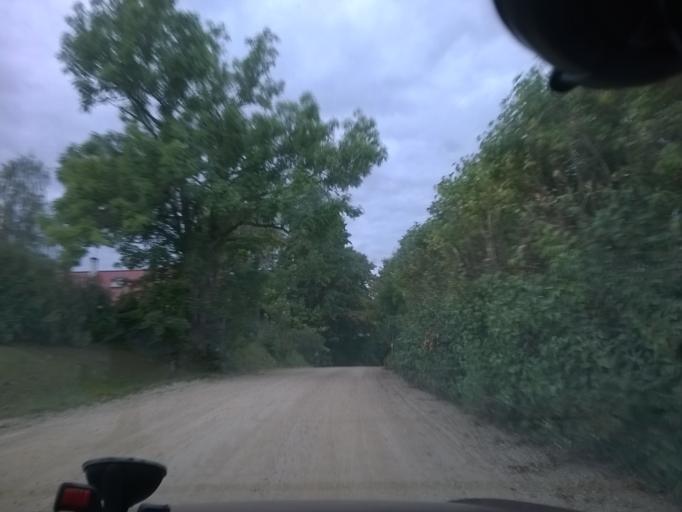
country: EE
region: Vorumaa
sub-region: Voru linn
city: Voru
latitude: 57.8134
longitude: 27.1576
